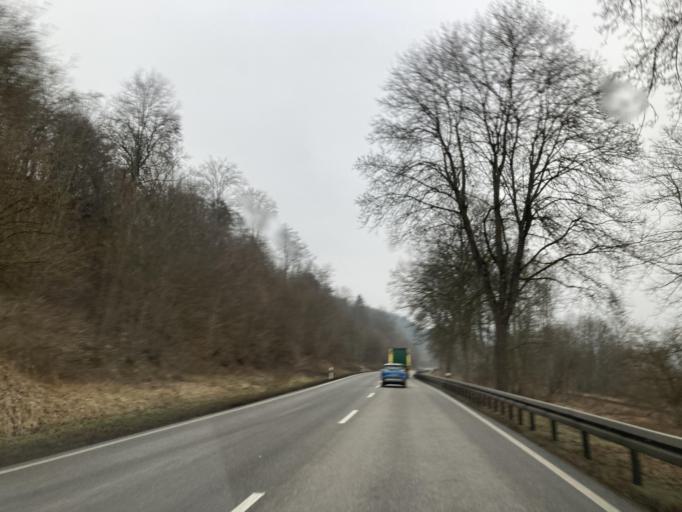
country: DE
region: Baden-Wuerttemberg
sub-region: Freiburg Region
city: Immendingen
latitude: 47.9423
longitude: 8.7596
